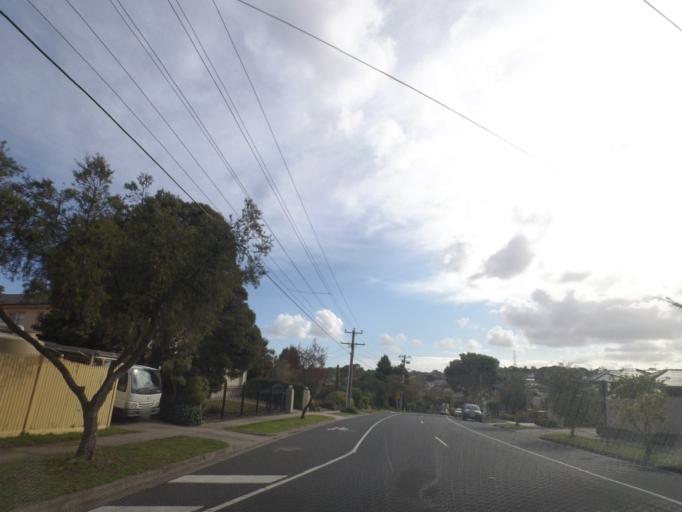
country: AU
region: Victoria
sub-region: Whitehorse
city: Vermont South
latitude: -37.8494
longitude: 145.1783
